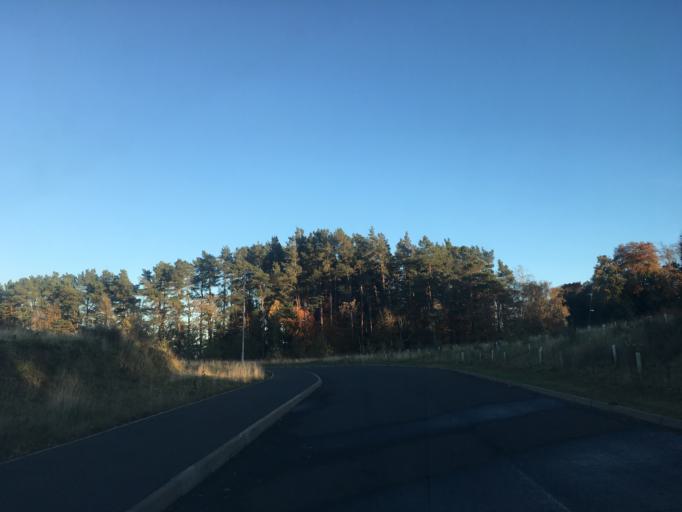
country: GB
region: Scotland
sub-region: Midlothian
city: Penicuik
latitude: 55.8629
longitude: -3.2044
